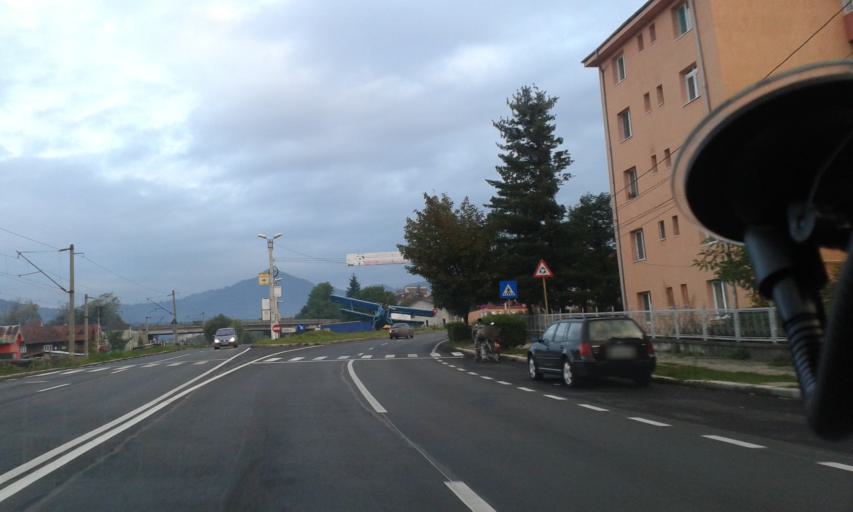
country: RO
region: Hunedoara
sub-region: Municipiul Petrosani
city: Petrosani
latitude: 45.4058
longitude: 23.3721
